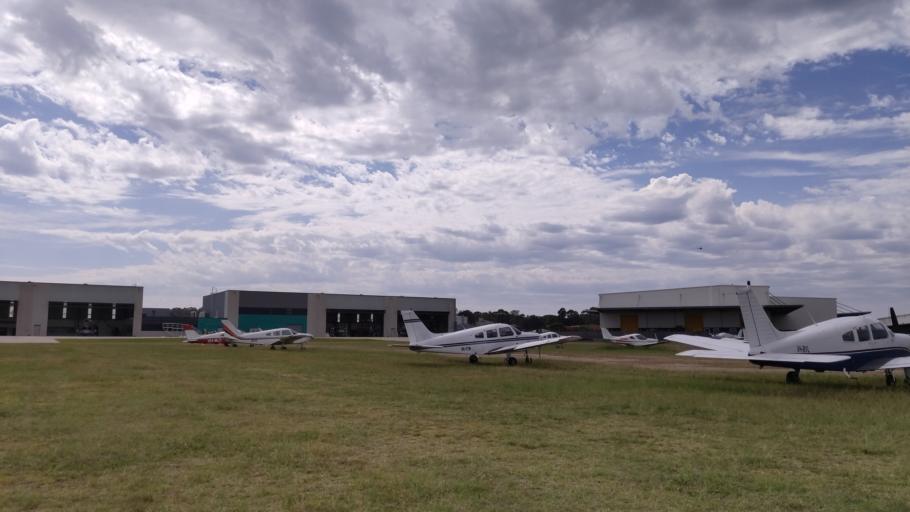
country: AU
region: New South Wales
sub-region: Bankstown
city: Milperra
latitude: -33.9206
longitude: 150.9928
